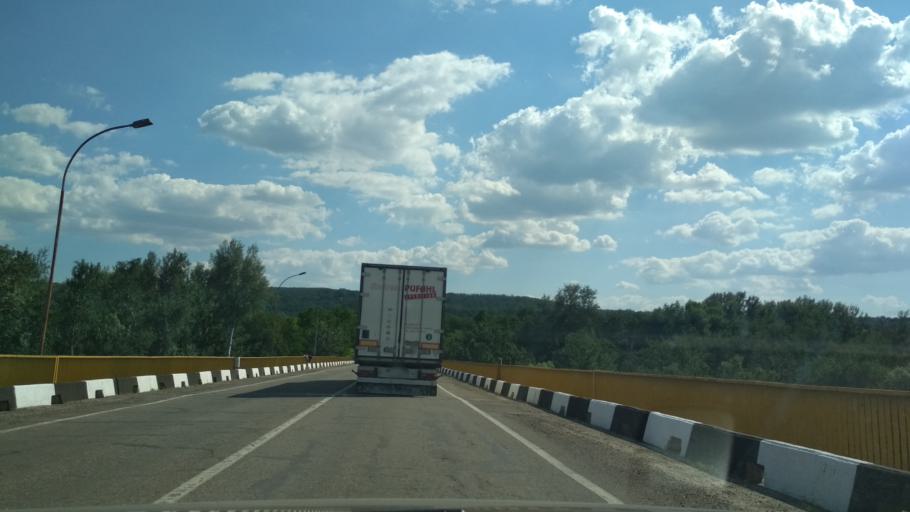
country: MD
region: Chisinau
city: Vadul lui Voda
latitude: 47.0892
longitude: 29.0913
